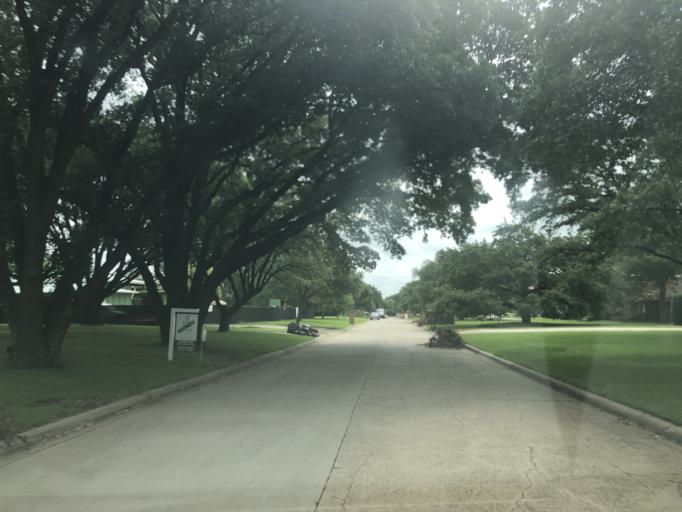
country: US
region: Texas
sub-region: Dallas County
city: University Park
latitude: 32.8898
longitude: -96.8322
